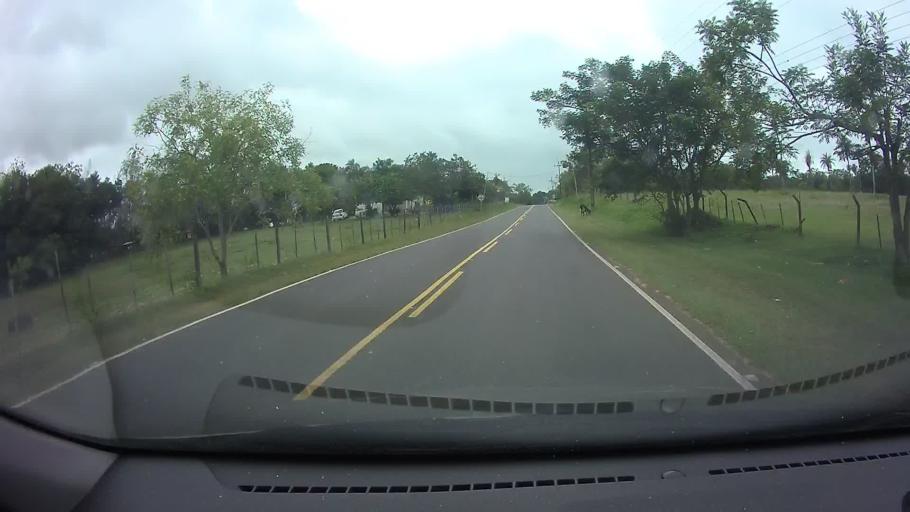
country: PY
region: Central
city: Nueva Italia
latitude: -25.6083
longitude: -57.4270
